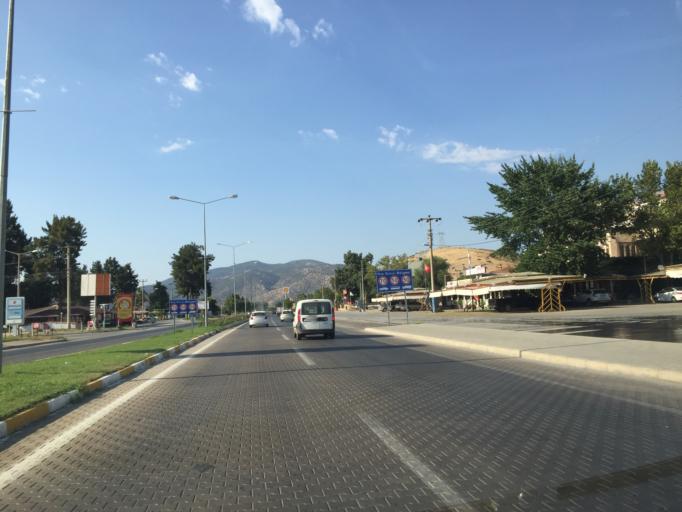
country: TR
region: Izmir
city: Selcuk
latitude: 37.9614
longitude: 27.3727
